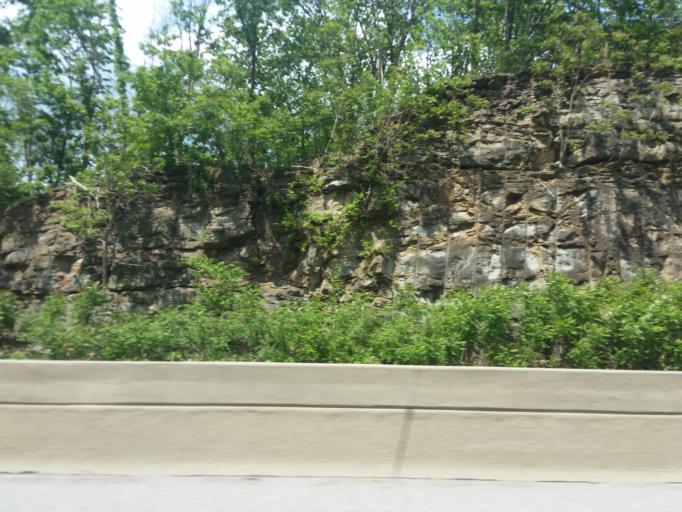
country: US
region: West Virginia
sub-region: Fayette County
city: Oak Hill
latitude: 37.9908
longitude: -81.3205
